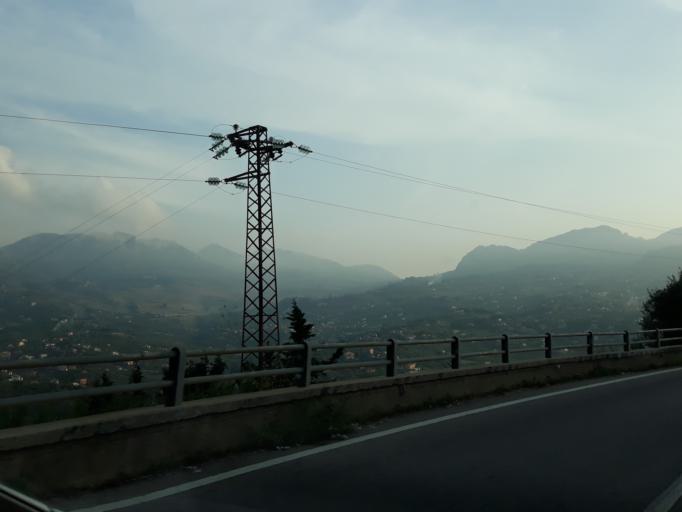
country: IT
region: Sicily
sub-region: Palermo
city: Cannizzaro-Favara
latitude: 38.0601
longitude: 13.2614
